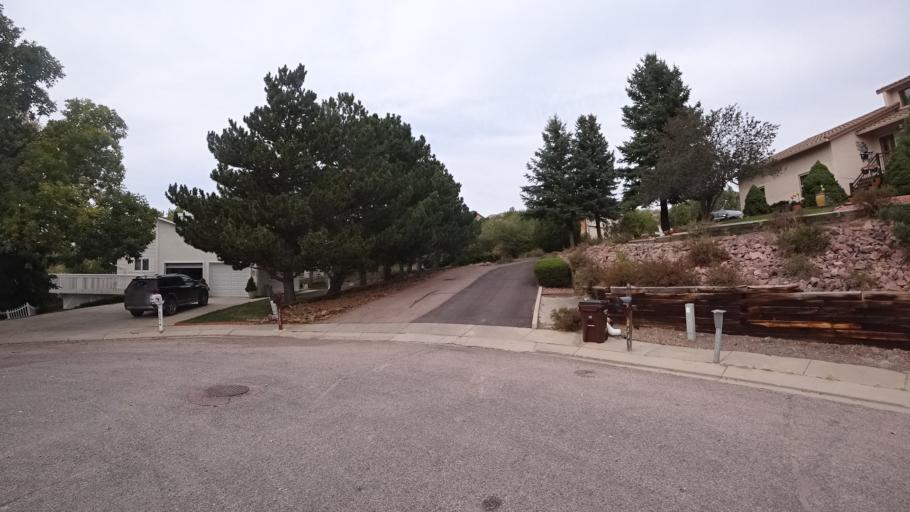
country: US
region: Colorado
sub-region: El Paso County
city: Cimarron Hills
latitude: 38.9086
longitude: -104.7265
